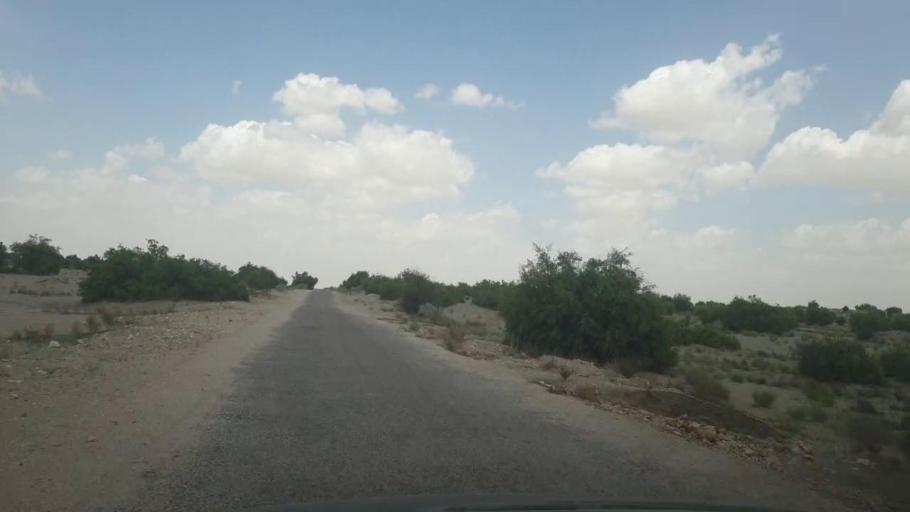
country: PK
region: Sindh
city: Kot Diji
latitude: 27.2223
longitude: 69.1065
